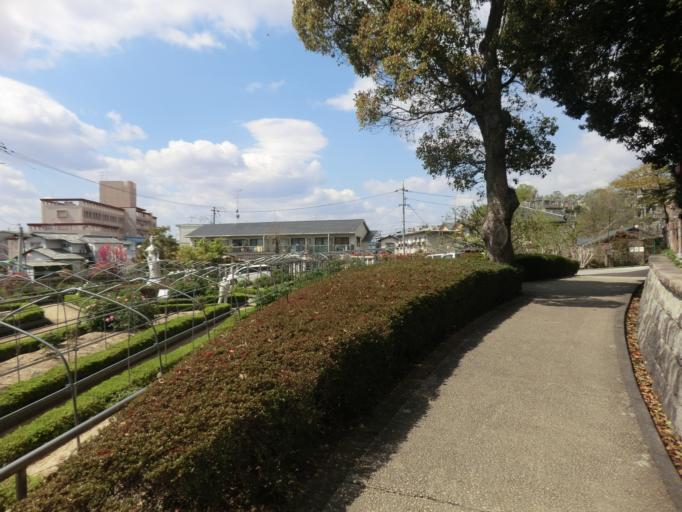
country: JP
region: Okayama
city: Okayama-shi
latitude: 34.6917
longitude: 133.9316
